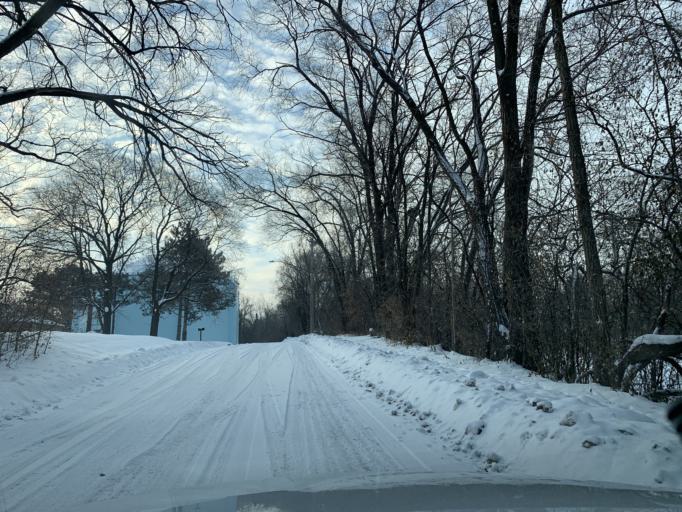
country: US
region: Minnesota
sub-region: Hennepin County
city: Saint Louis Park
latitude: 44.9238
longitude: -93.3542
